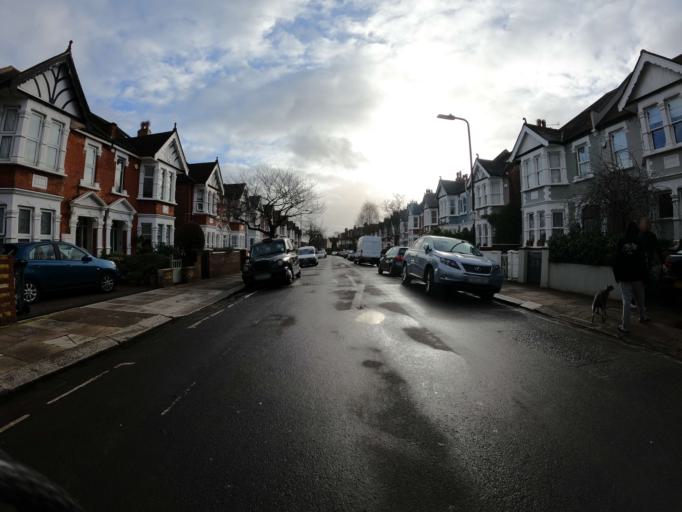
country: GB
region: England
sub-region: Greater London
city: Acton
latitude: 51.5124
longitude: -0.2637
